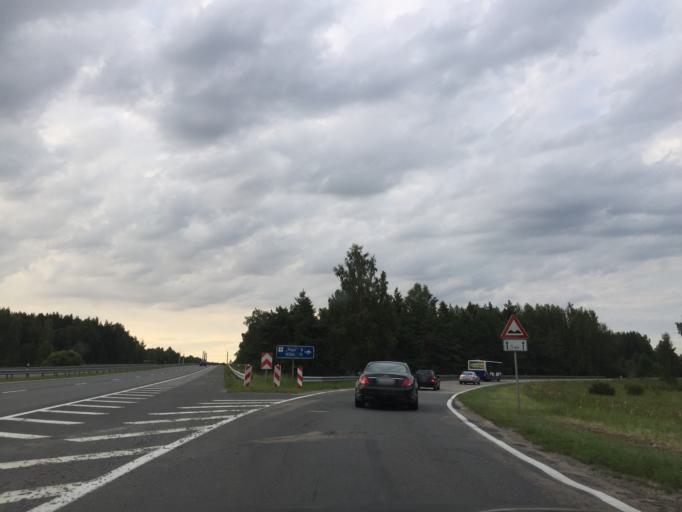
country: LV
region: Babite
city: Pinki
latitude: 56.9493
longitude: 23.9256
